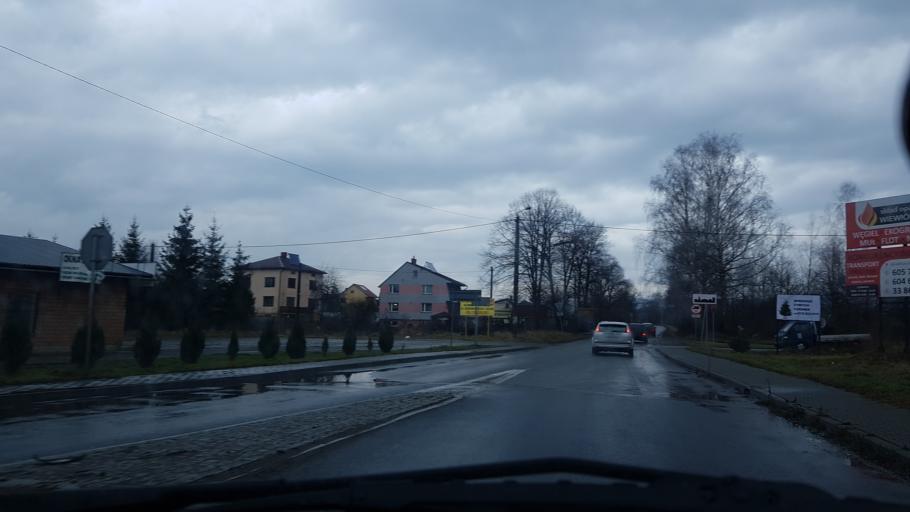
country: PL
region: Silesian Voivodeship
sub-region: Powiat zywiecki
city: Lekawica
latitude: 49.7113
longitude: 19.2373
